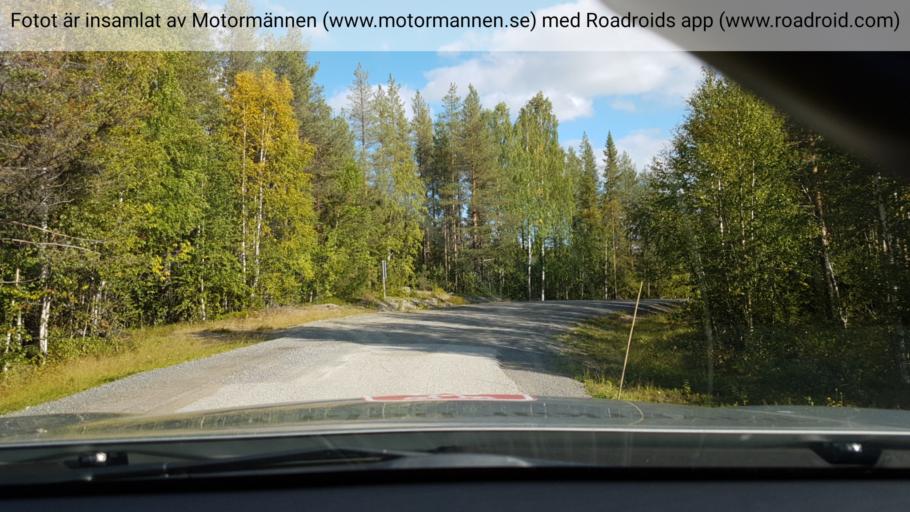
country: SE
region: Vaesterbotten
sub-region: Sorsele Kommun
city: Sorsele
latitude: 65.4888
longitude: 17.5761
